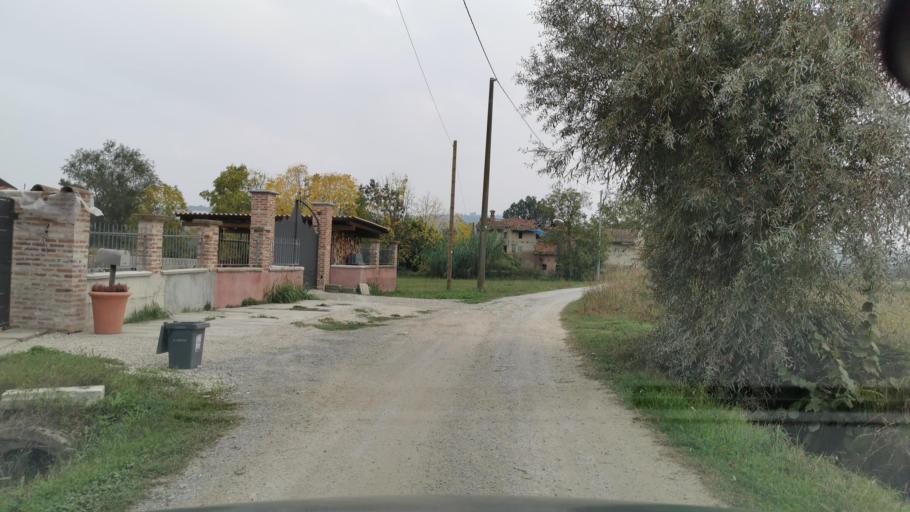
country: IT
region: Piedmont
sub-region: Provincia di Cuneo
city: Cinzano
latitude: 44.6921
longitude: 7.9124
